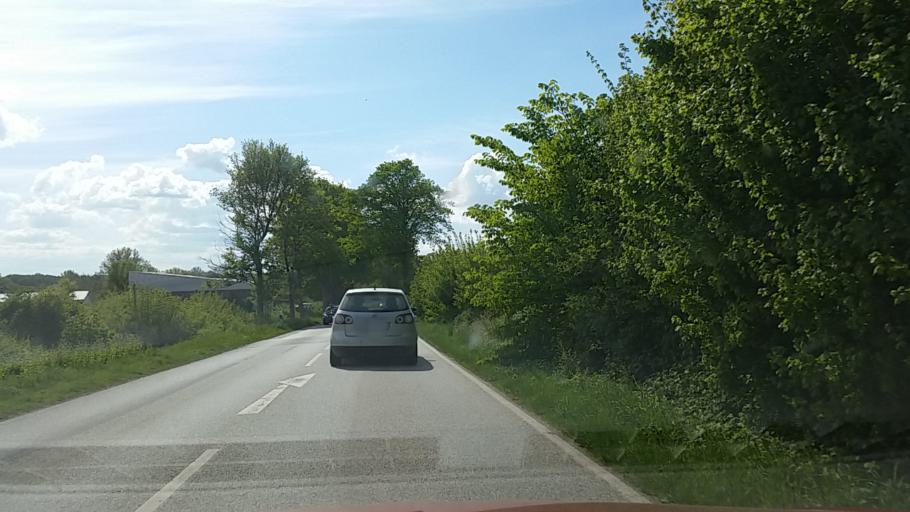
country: DE
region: Schleswig-Holstein
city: Reinfeld
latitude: 53.8220
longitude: 10.4782
